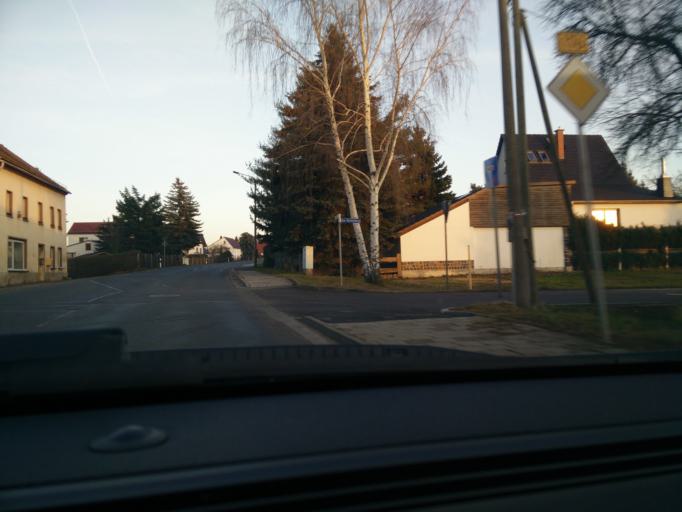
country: DE
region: Saxony
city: Bad Lausick
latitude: 51.1435
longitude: 12.6256
